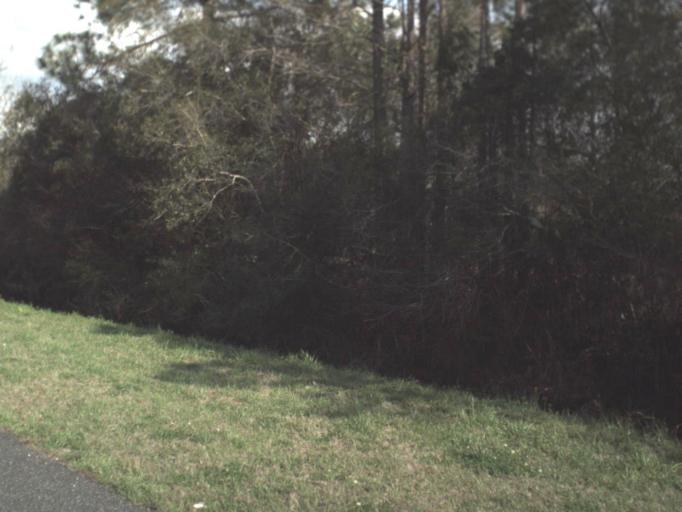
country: US
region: Florida
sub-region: Bay County
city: Youngstown
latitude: 30.2828
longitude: -85.5089
